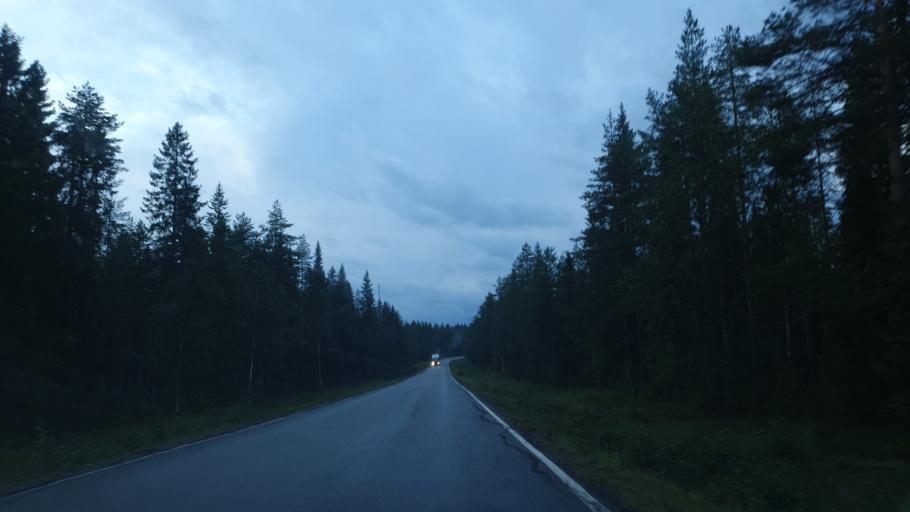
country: FI
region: Kainuu
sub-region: Kehys-Kainuu
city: Kuhmo
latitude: 63.9575
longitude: 29.7067
